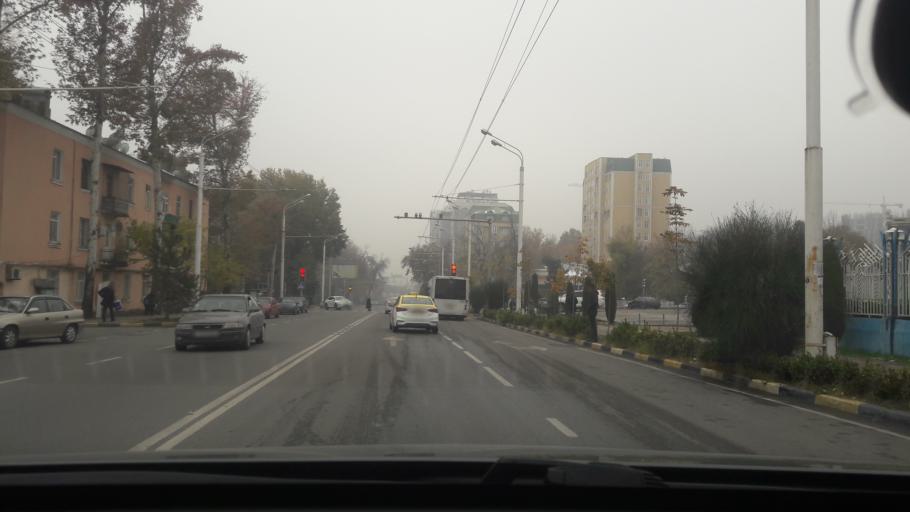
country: TJ
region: Dushanbe
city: Dushanbe
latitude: 38.5732
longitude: 68.8014
